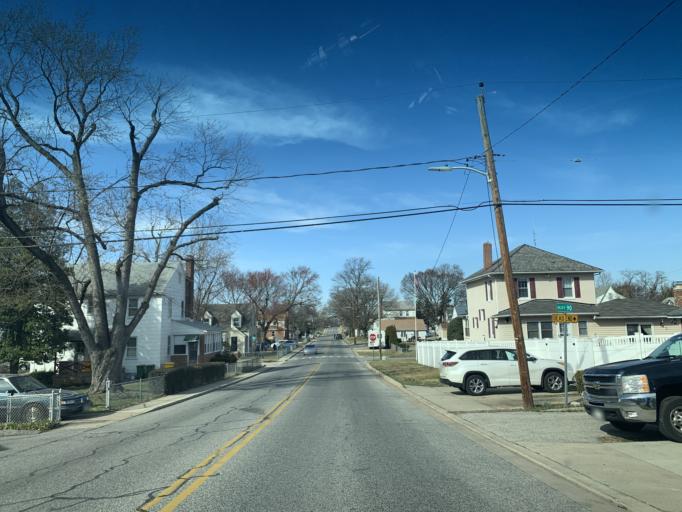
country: US
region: Maryland
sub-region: Anne Arundel County
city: Brooklyn Park
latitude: 39.2236
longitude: -76.6153
